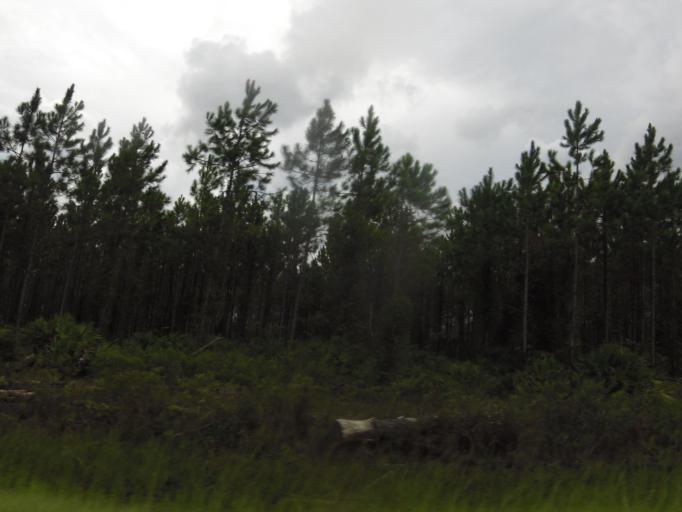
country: US
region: Florida
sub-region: Baker County
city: Macclenny
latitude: 30.5183
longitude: -82.1269
